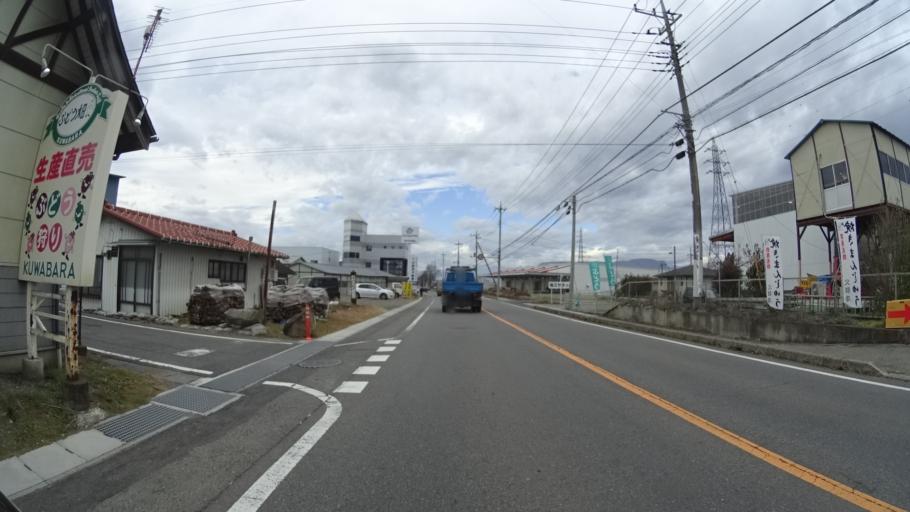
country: JP
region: Gunma
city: Numata
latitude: 36.6645
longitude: 139.1179
